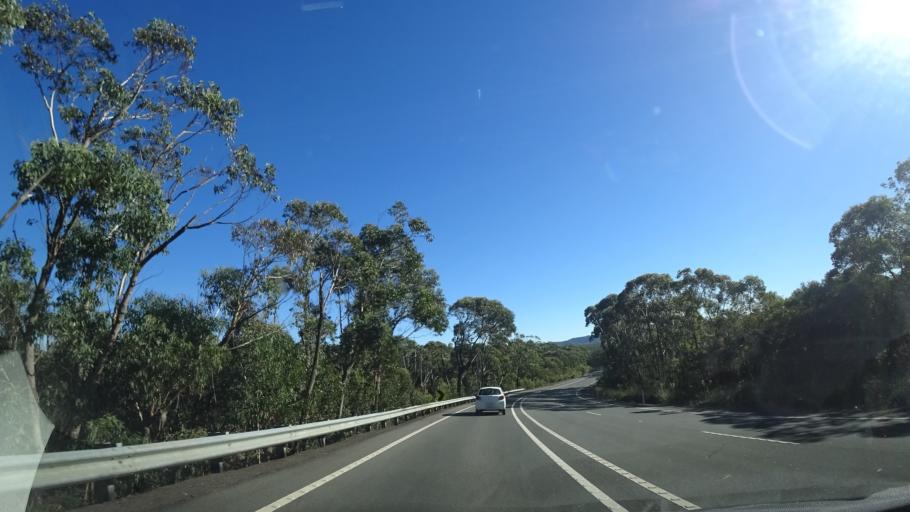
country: AU
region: New South Wales
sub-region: Blue Mountains Municipality
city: Blackheath
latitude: -33.5607
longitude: 150.3432
